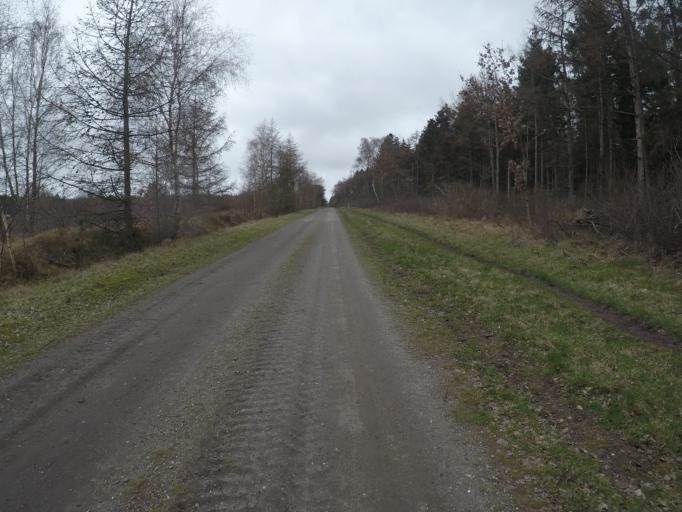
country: DE
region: Lower Saxony
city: Nordholz
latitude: 53.8293
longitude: 8.6129
